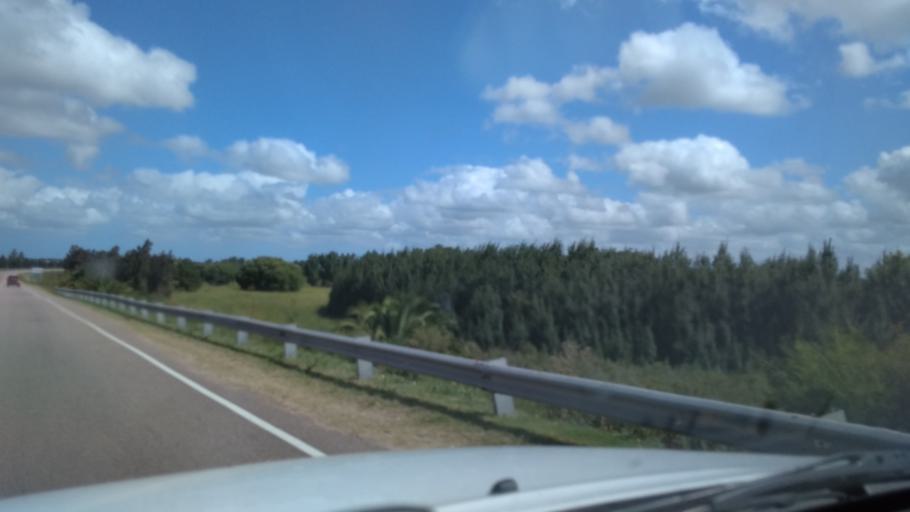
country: UY
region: Canelones
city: Sauce
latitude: -34.6411
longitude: -56.0521
